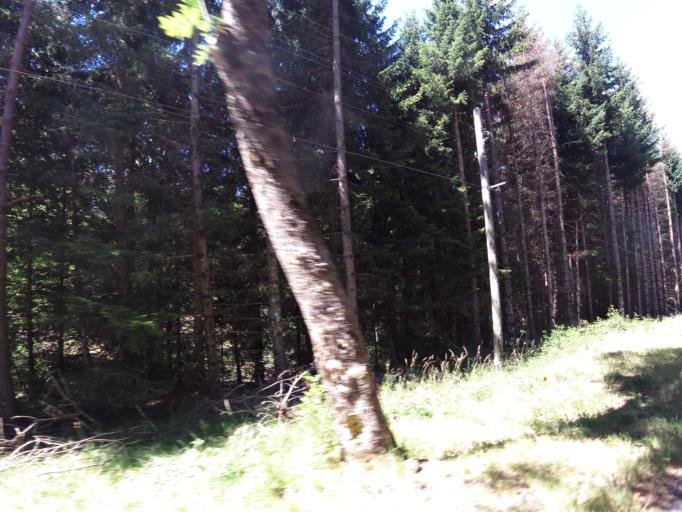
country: FR
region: Languedoc-Roussillon
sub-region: Departement de la Lozere
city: Meyrueis
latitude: 44.1074
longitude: 3.4860
